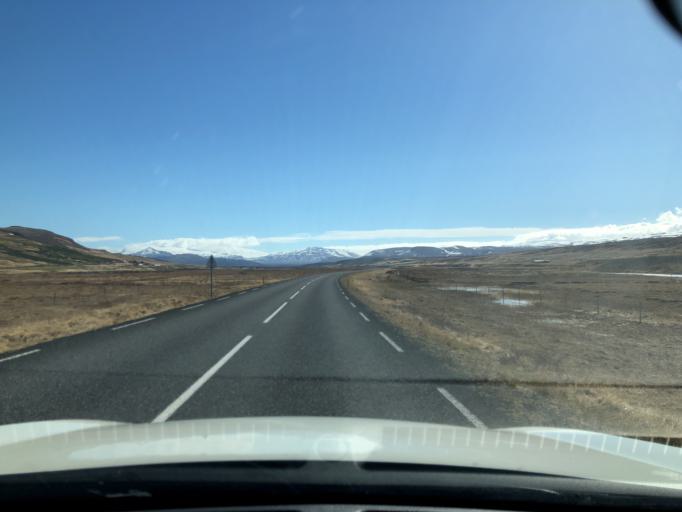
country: IS
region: South
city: Hveragerdi
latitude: 64.7025
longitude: -21.1153
